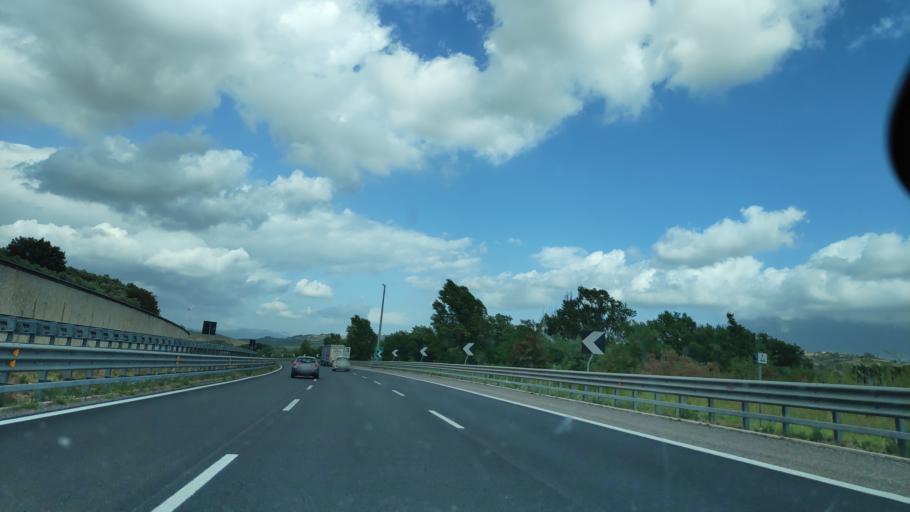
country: IT
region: Campania
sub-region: Provincia di Salerno
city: Quadrivio
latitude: 40.6135
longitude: 15.1480
